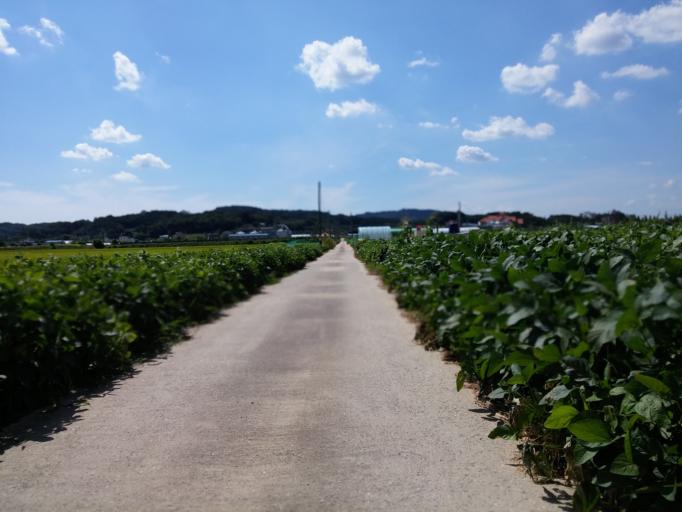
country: KR
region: Chungcheongbuk-do
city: Cheongju-si
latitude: 36.5927
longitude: 127.4957
